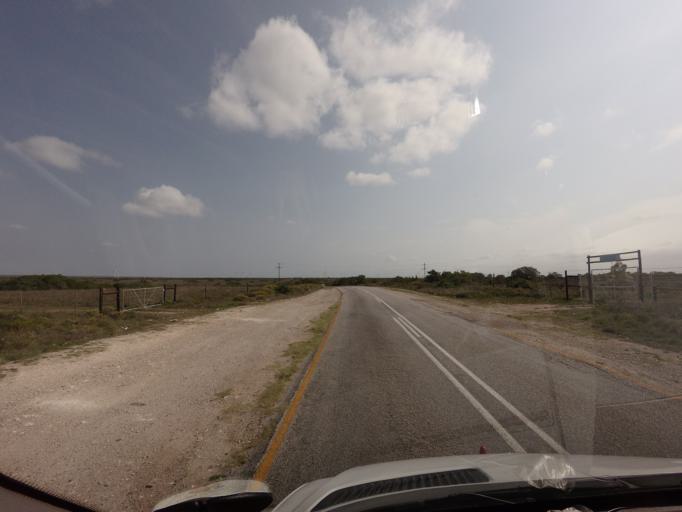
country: ZA
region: Eastern Cape
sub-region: Nelson Mandela Bay Metropolitan Municipality
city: Uitenhage
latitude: -33.7027
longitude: 25.5888
